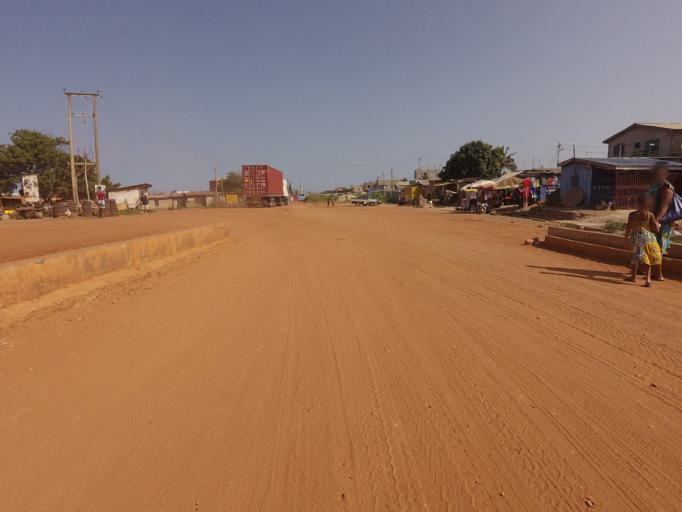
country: GH
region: Greater Accra
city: Teshi Old Town
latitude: 5.5803
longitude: -0.1126
